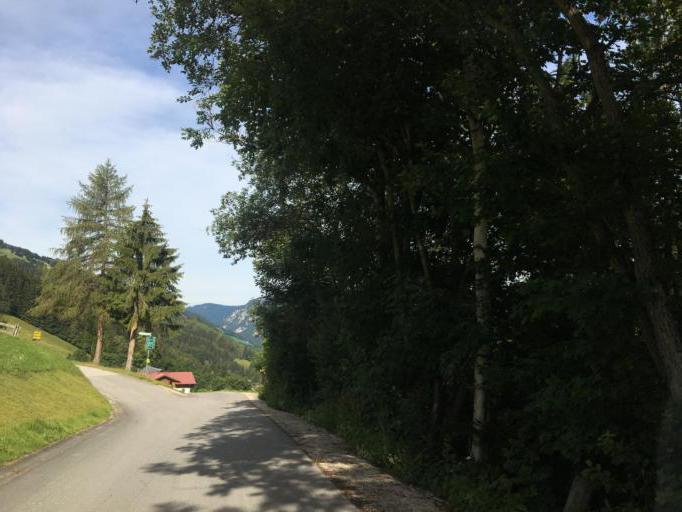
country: AT
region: Styria
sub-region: Politischer Bezirk Liezen
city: Schladming
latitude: 47.3852
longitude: 13.6620
